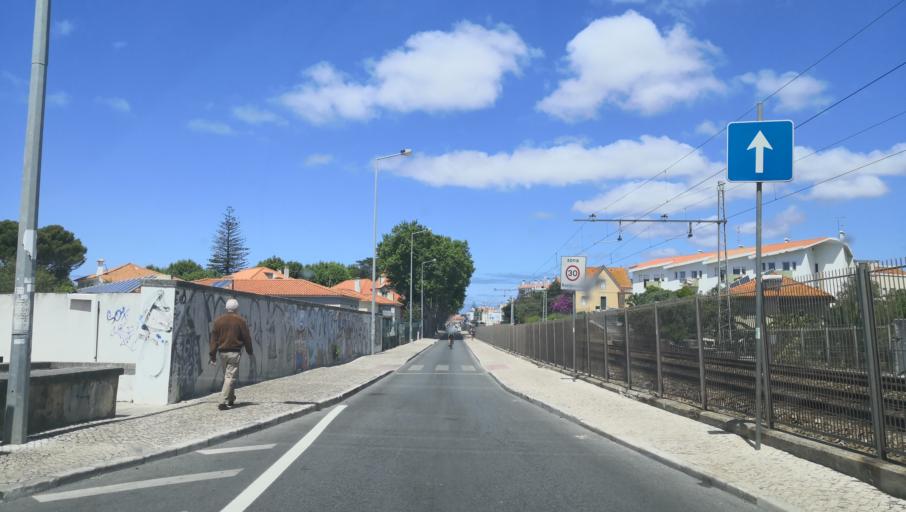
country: PT
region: Lisbon
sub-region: Cascais
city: Parede
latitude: 38.6879
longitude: -9.3516
